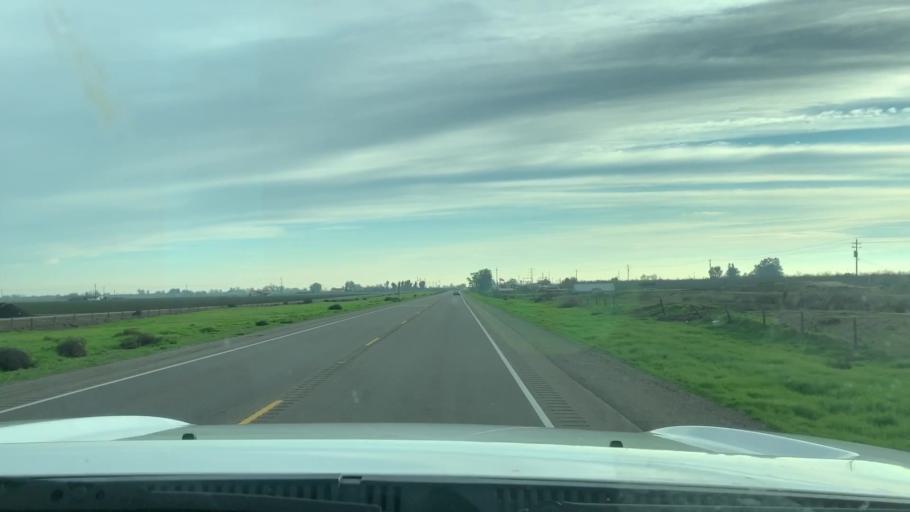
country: US
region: California
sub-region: Fresno County
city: Riverdale
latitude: 36.4526
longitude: -119.7971
